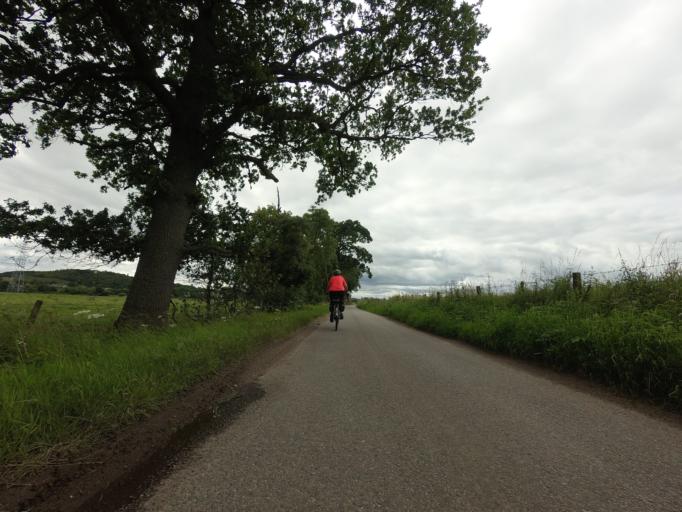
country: GB
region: Scotland
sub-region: Moray
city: Forres
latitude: 57.6210
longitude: -3.6138
